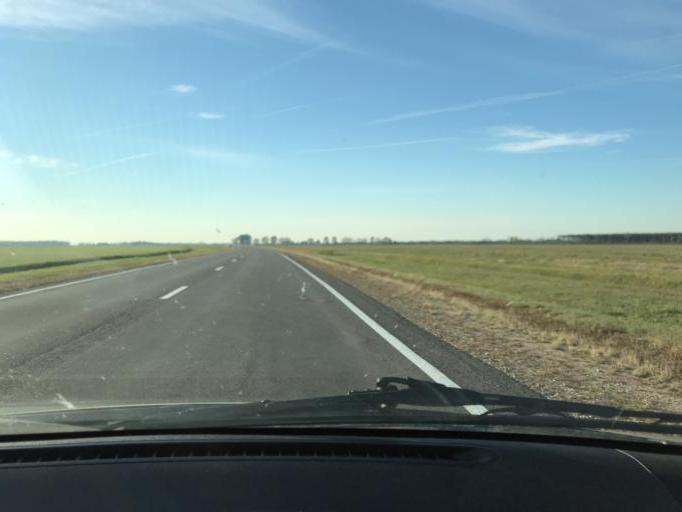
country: BY
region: Brest
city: Antopal'
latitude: 52.2268
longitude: 24.8151
